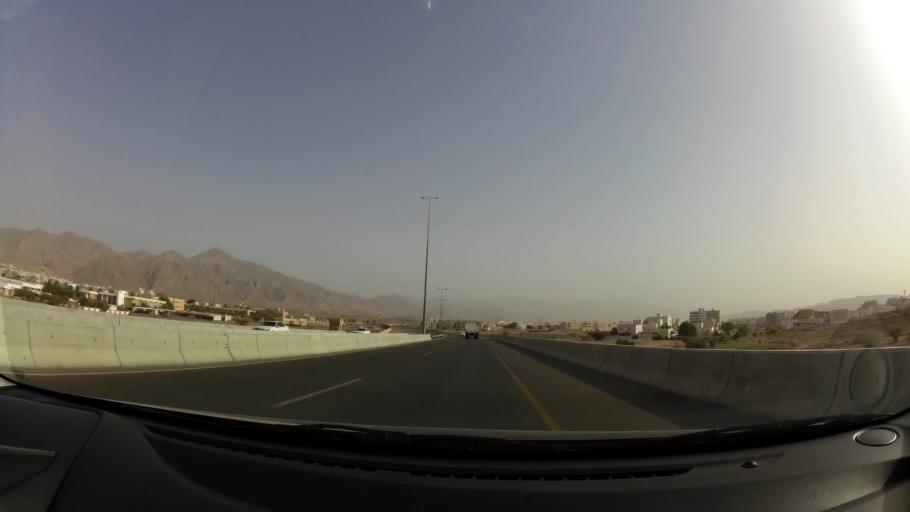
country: OM
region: Muhafazat Masqat
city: Bawshar
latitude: 23.5519
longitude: 58.3670
